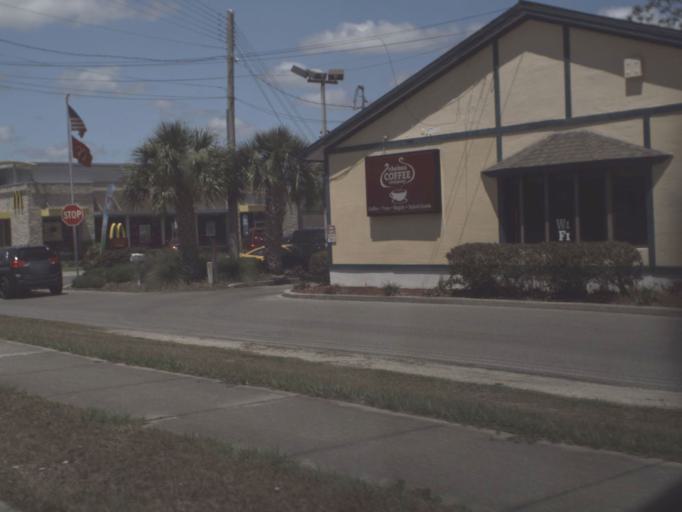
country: US
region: Florida
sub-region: Marion County
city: Ocala
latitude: 29.1950
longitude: -82.0910
